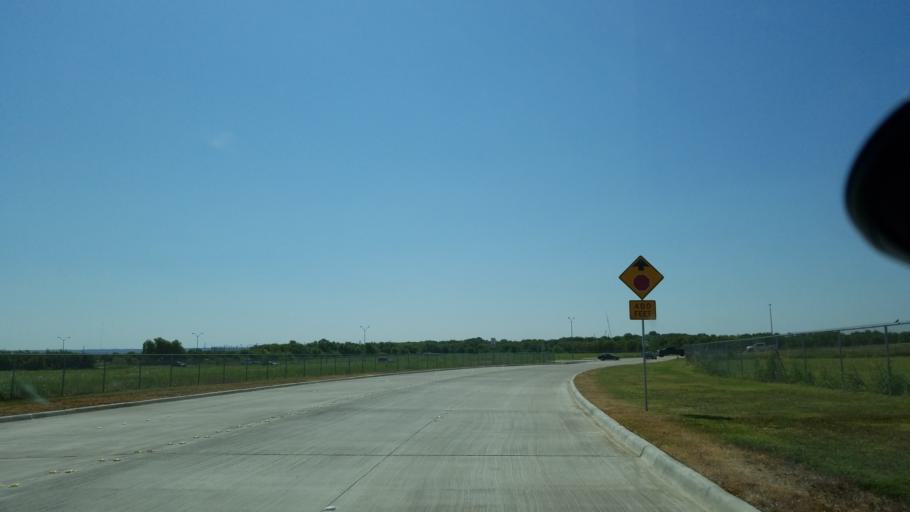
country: US
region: Texas
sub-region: Tarrant County
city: Mansfield
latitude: 32.5601
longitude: -97.1001
